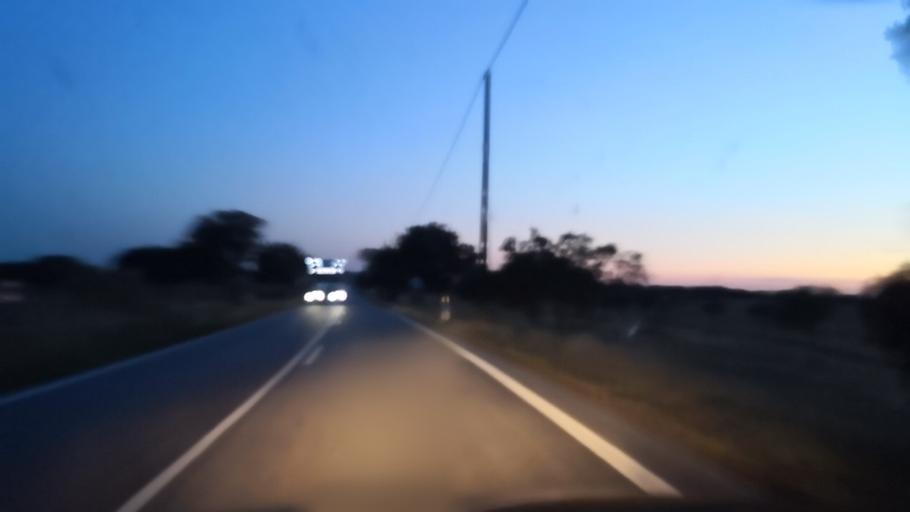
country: ES
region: Extremadura
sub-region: Provincia de Caceres
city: Piedras Albas
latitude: 39.8572
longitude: -7.0437
